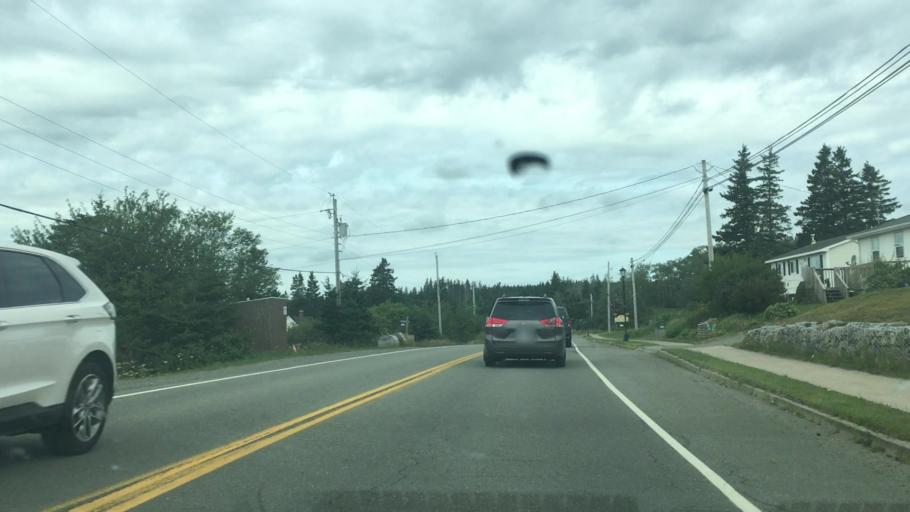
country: CA
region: Nova Scotia
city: Princeville
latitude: 45.6545
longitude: -60.8930
